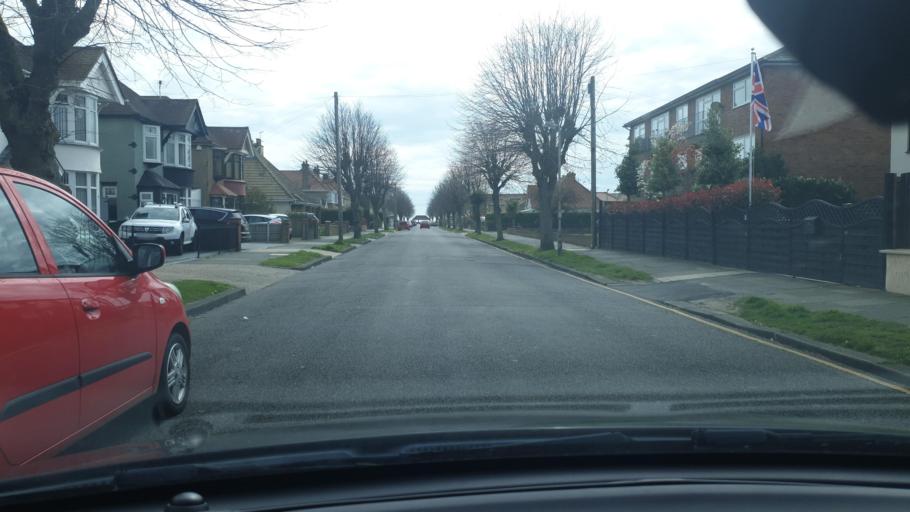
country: GB
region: England
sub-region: Essex
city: Clacton-on-Sea
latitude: 51.8012
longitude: 1.1828
